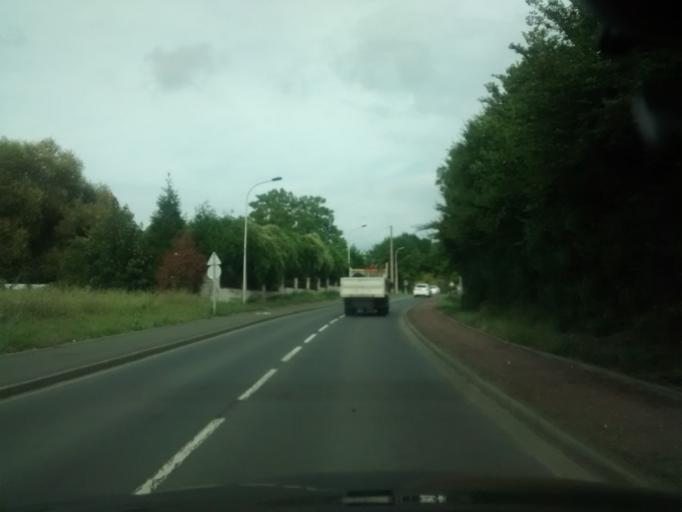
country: FR
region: Lower Normandy
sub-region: Departement du Calvados
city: Deauville
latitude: 49.3271
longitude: 0.0718
